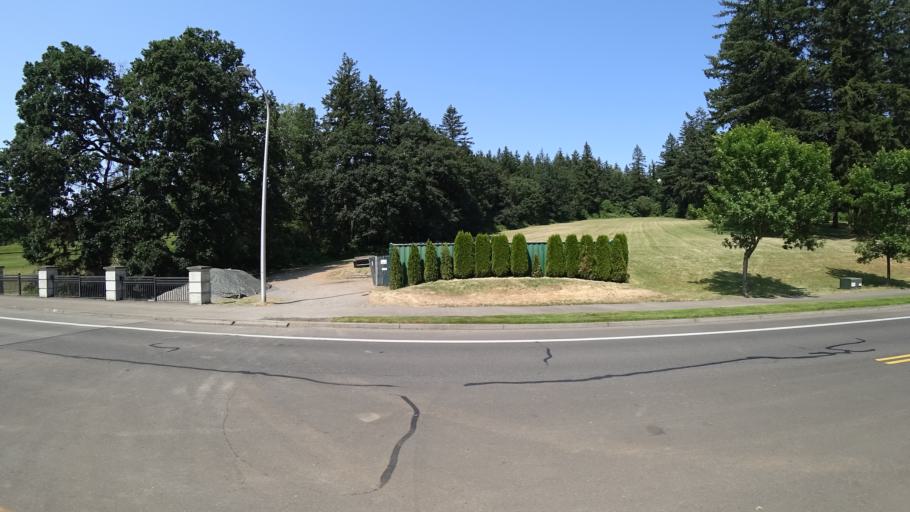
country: US
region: Oregon
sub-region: Clackamas County
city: Happy Valley
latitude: 45.4406
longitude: -122.5563
